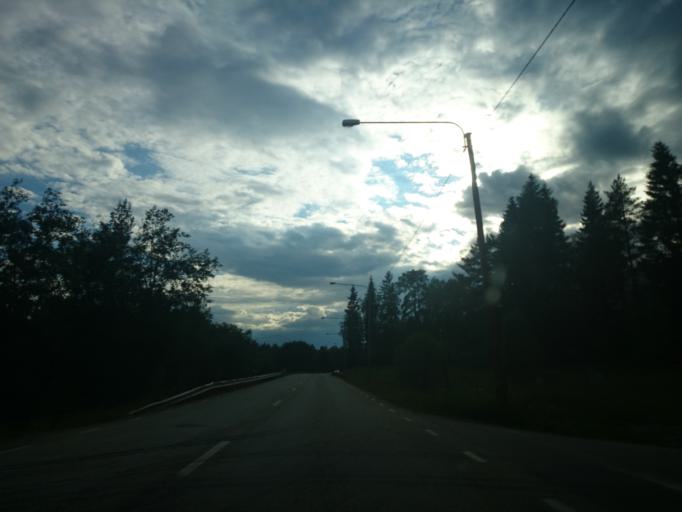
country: SE
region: Vaesternorrland
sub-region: Haernoesands Kommun
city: Haernoesand
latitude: 62.6372
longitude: 17.8468
